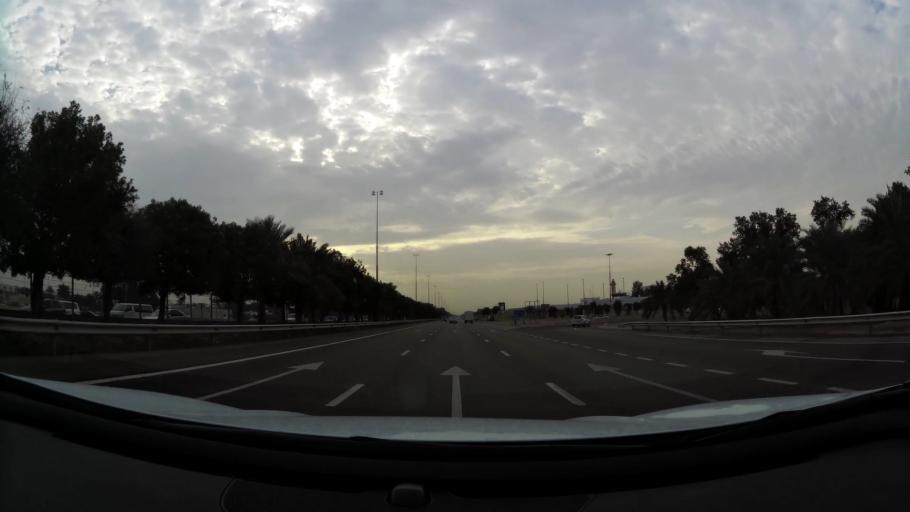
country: AE
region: Abu Dhabi
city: Abu Dhabi
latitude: 24.2954
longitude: 54.6287
